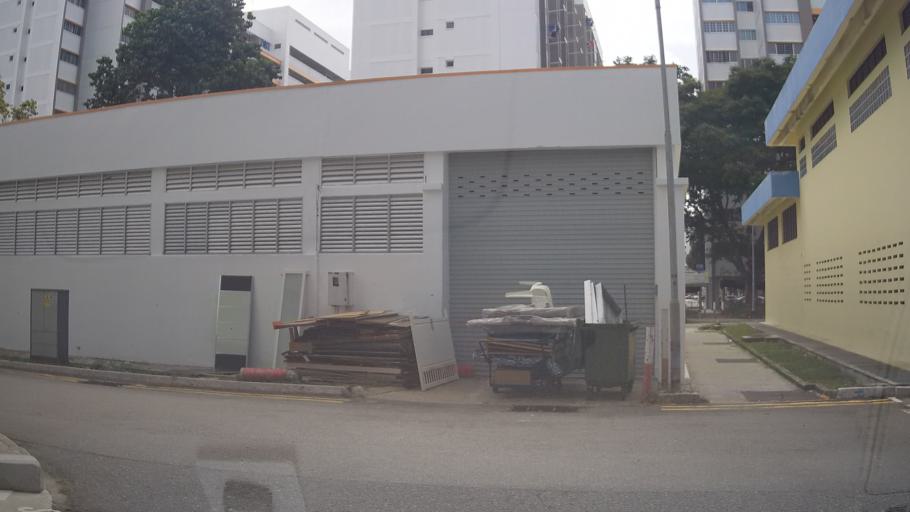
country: SG
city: Singapore
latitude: 1.3471
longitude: 103.9356
